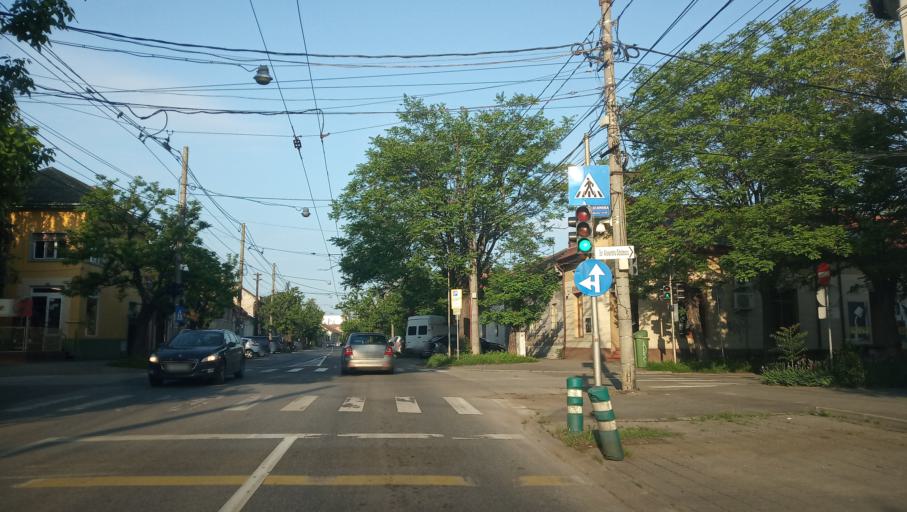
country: RO
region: Timis
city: Timisoara
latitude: 45.7407
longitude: 21.2231
